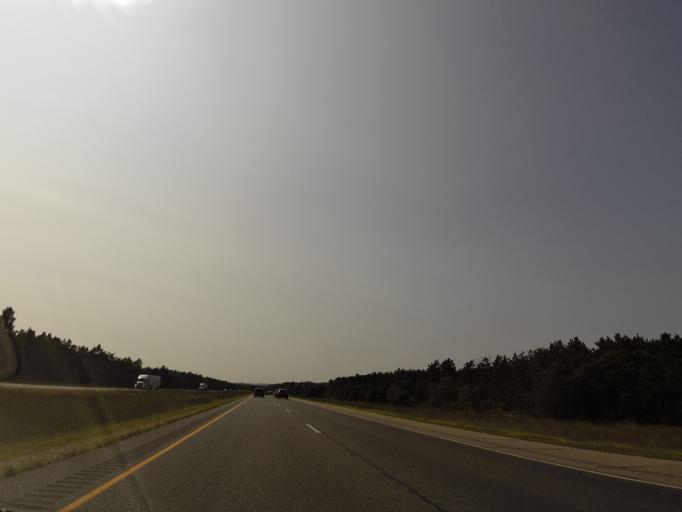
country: US
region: Wisconsin
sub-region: Monroe County
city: Tomah
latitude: 43.9397
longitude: -90.6358
